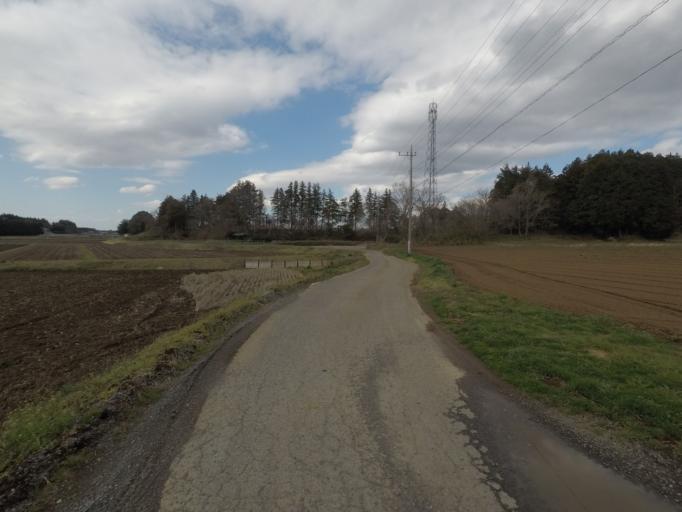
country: JP
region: Ibaraki
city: Ushiku
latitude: 36.0092
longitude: 140.1177
